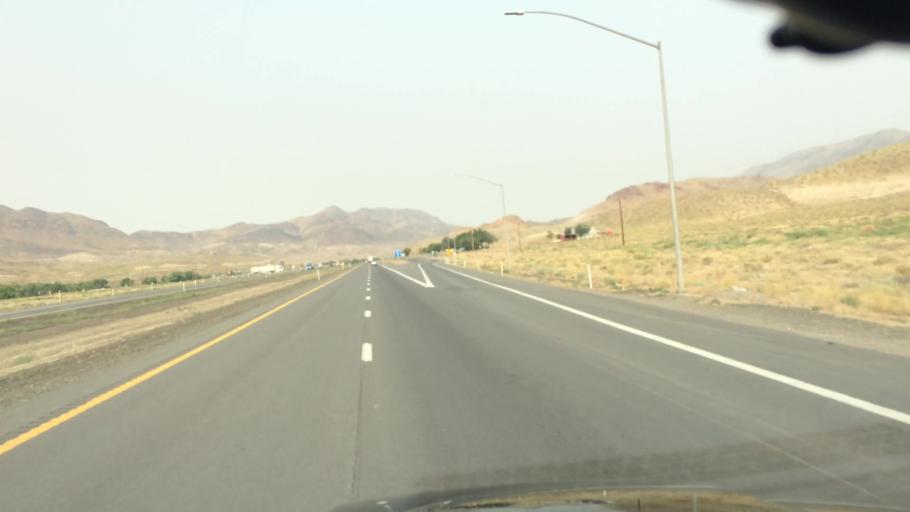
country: US
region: Nevada
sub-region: Lyon County
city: Fernley
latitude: 39.6047
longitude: -119.3299
